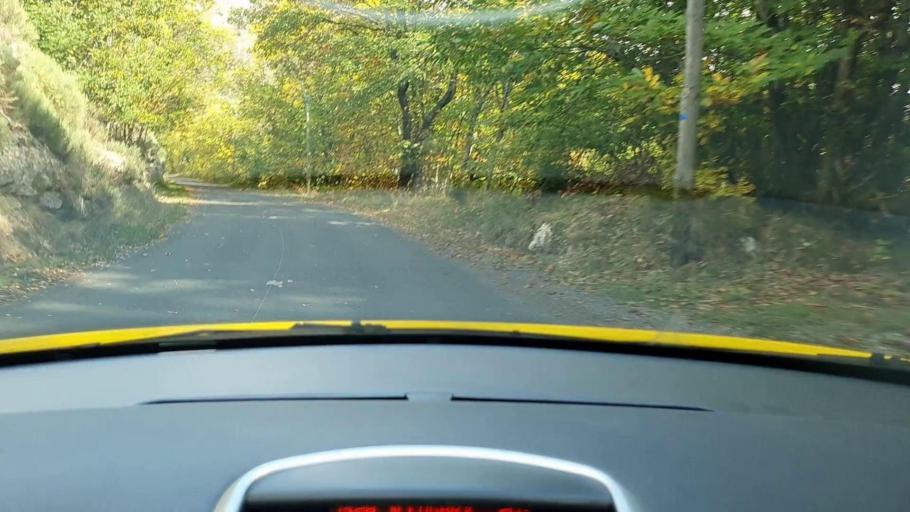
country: FR
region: Languedoc-Roussillon
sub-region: Departement de la Lozere
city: Meyrueis
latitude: 44.0685
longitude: 3.4482
